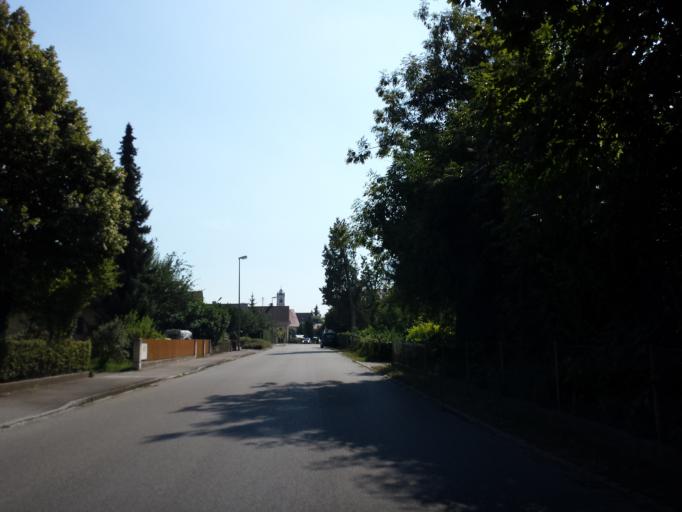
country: DE
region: Bavaria
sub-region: Swabia
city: Turkheim
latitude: 48.0680
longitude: 10.6423
